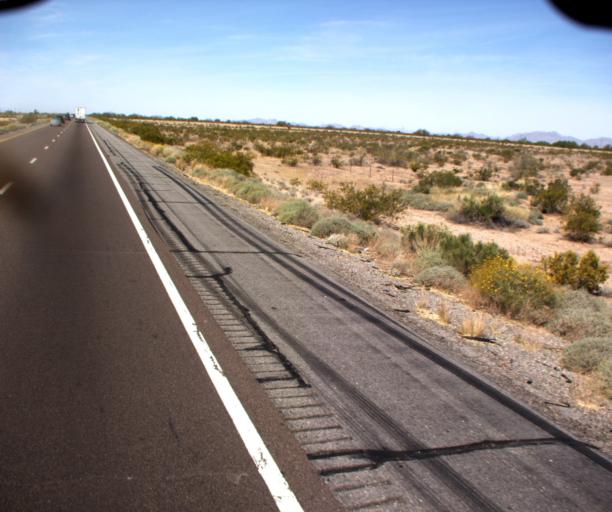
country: US
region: Arizona
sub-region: La Paz County
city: Salome
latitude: 33.5566
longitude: -113.2695
